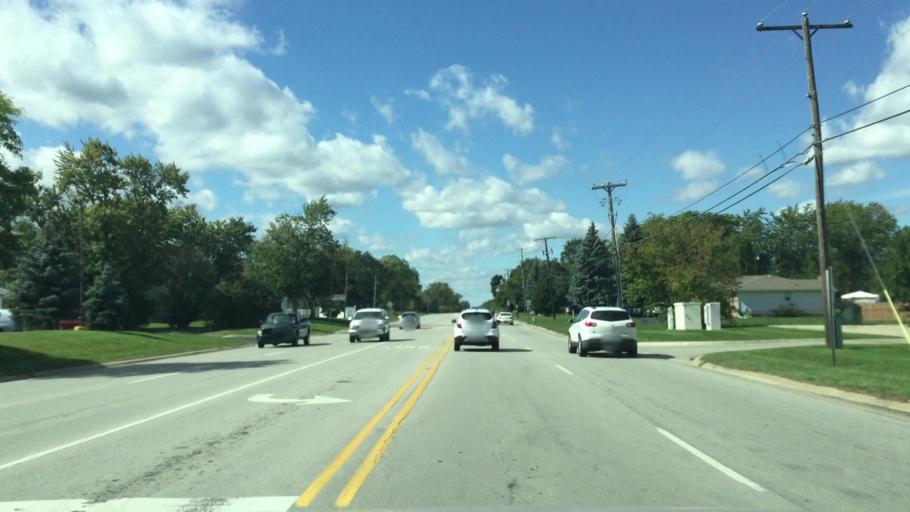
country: US
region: Michigan
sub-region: Genesee County
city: Flint
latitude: 42.9439
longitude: -83.7321
